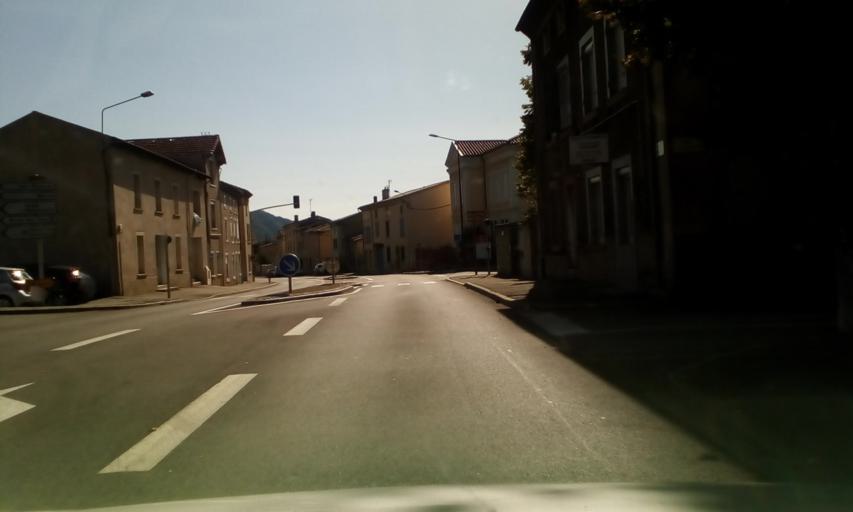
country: FR
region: Rhone-Alpes
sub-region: Departement de l'Ardeche
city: Saint-Jean-de-Muzols
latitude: 45.1212
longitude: 4.8196
